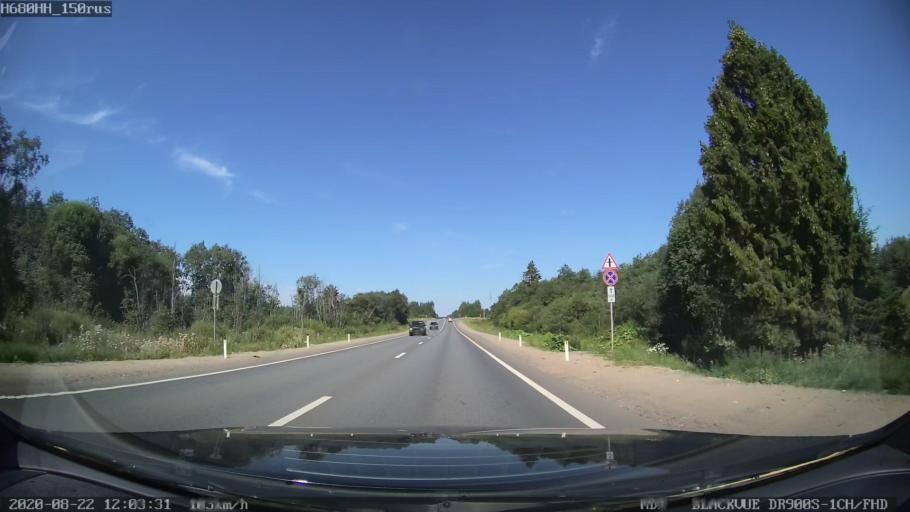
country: RU
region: Tverskaya
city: Rameshki
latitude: 57.2559
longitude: 36.0841
